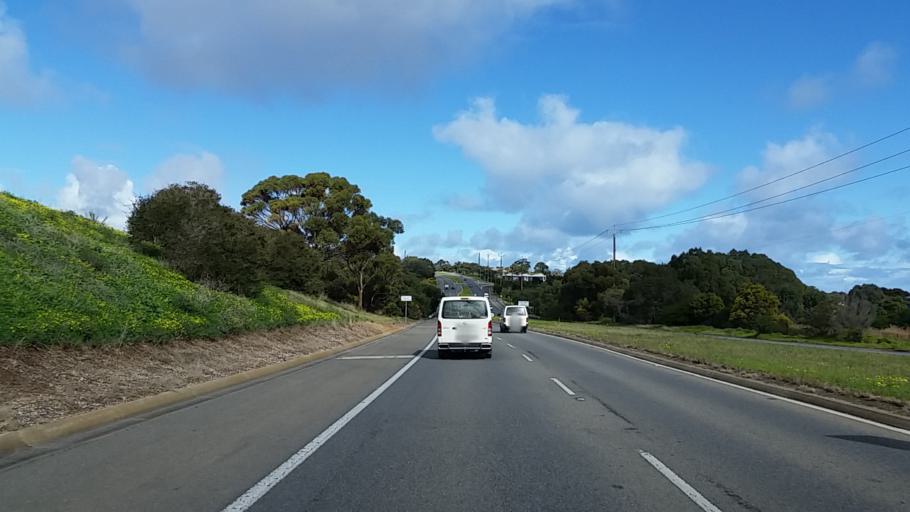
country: AU
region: South Australia
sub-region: Onkaparinga
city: Morphett Vale
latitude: -35.1216
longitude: 138.4882
